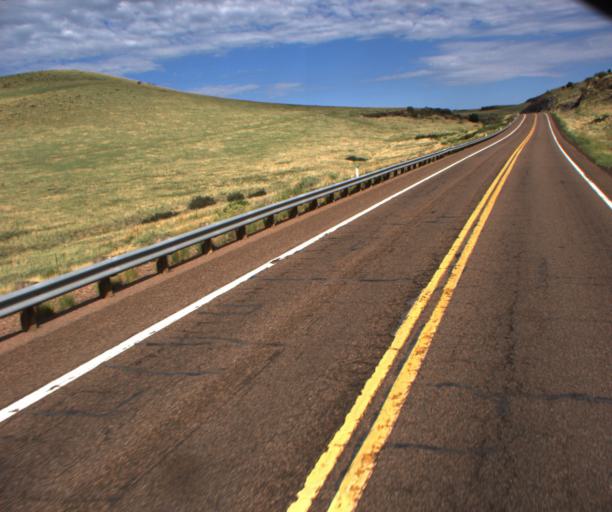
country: US
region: Arizona
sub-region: Apache County
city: Springerville
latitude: 34.2088
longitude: -109.4247
